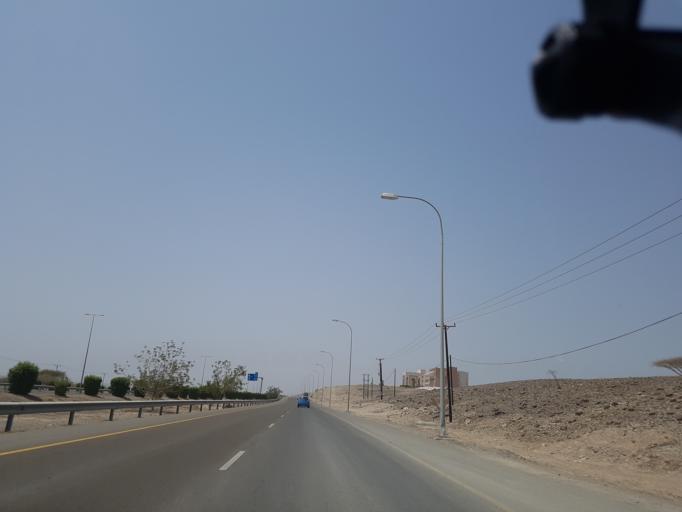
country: OM
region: Al Batinah
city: Al Liwa'
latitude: 24.4113
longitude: 56.5946
